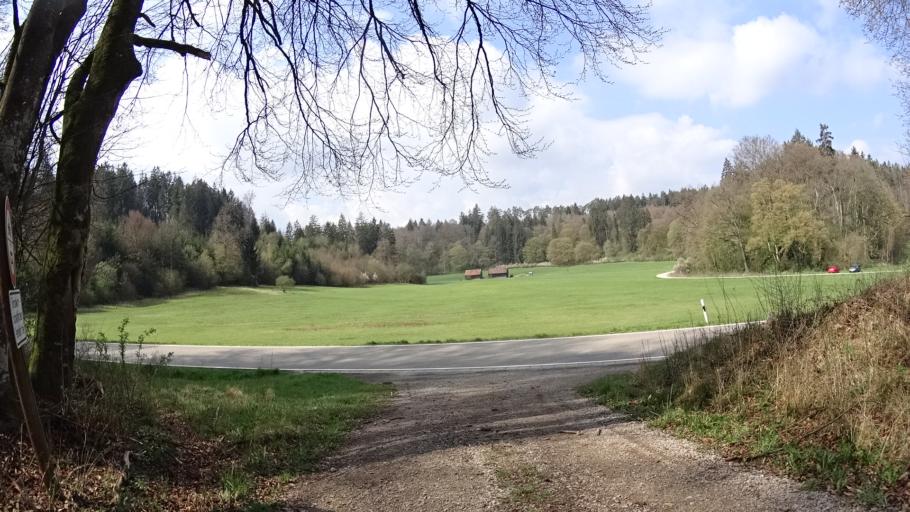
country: DE
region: Bavaria
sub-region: Upper Bavaria
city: Bohmfeld
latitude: 48.8922
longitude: 11.3710
